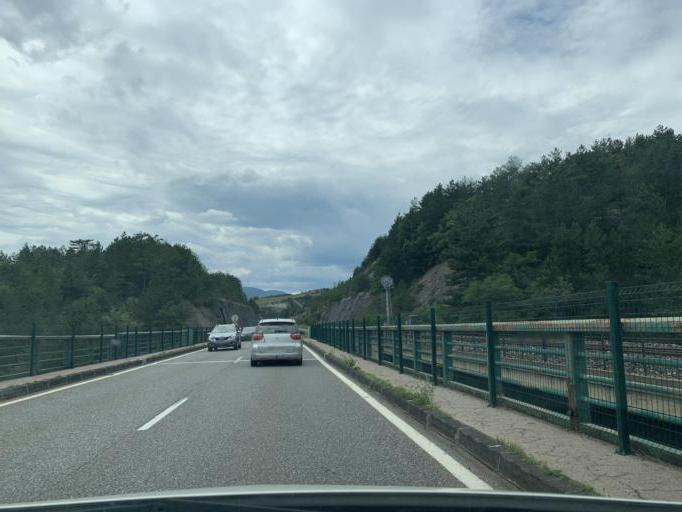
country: FR
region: Provence-Alpes-Cote d'Azur
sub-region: Departement des Hautes-Alpes
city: Chorges
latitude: 44.5303
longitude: 6.3672
